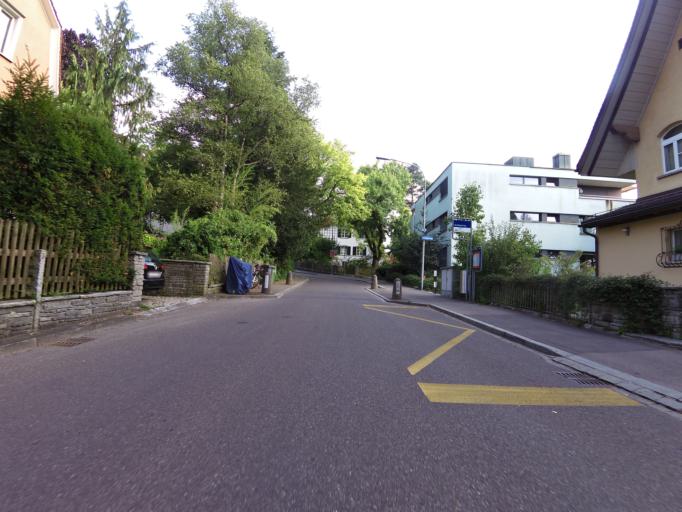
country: CH
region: Zurich
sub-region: Bezirk Zuerich
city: Zuerich (Kreis 6) / Oberstrass
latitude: 47.3901
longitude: 8.5509
